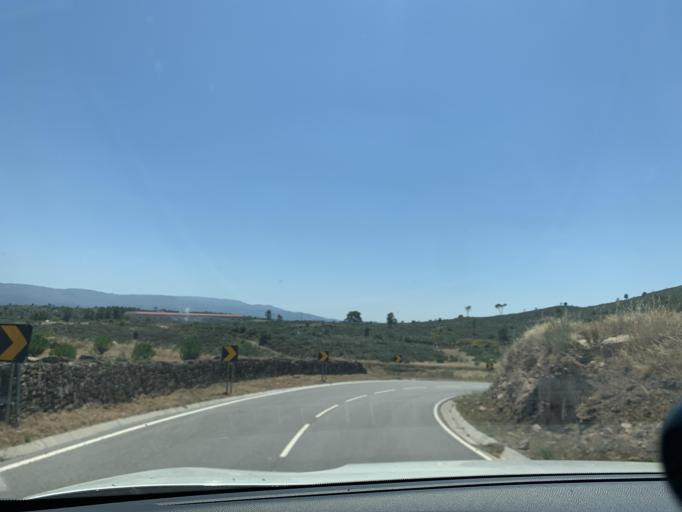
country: PT
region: Viseu
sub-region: Mangualde
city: Mangualde
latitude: 40.5715
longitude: -7.6482
